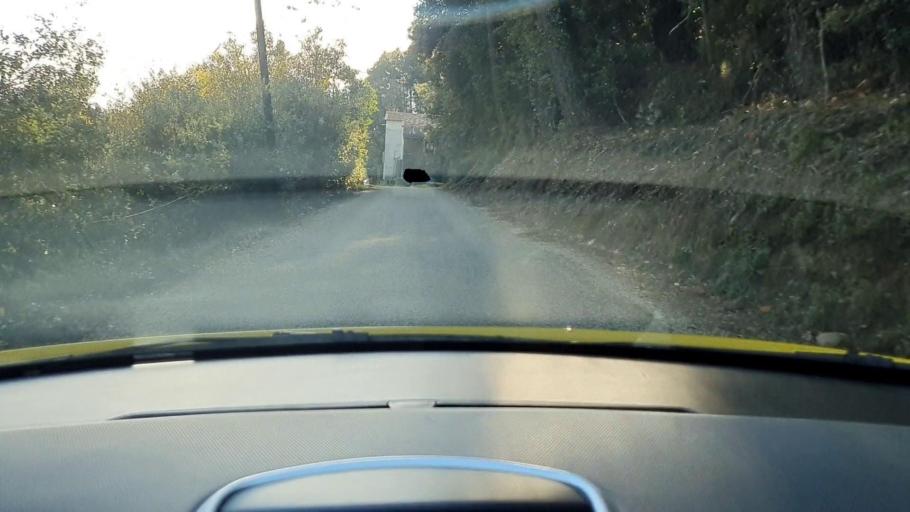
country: FR
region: Languedoc-Roussillon
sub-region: Departement du Gard
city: Branoux-les-Taillades
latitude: 44.2420
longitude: 3.9837
